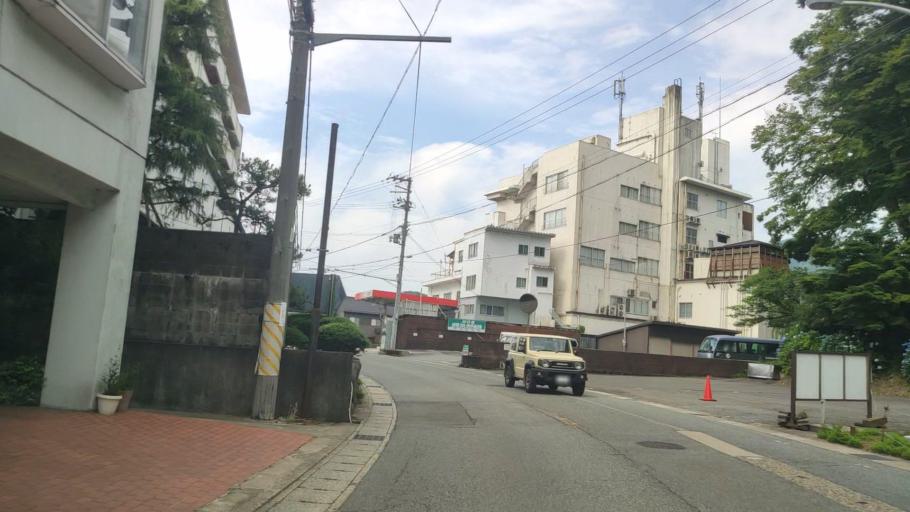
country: JP
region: Hyogo
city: Toyooka
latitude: 35.6275
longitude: 134.8151
